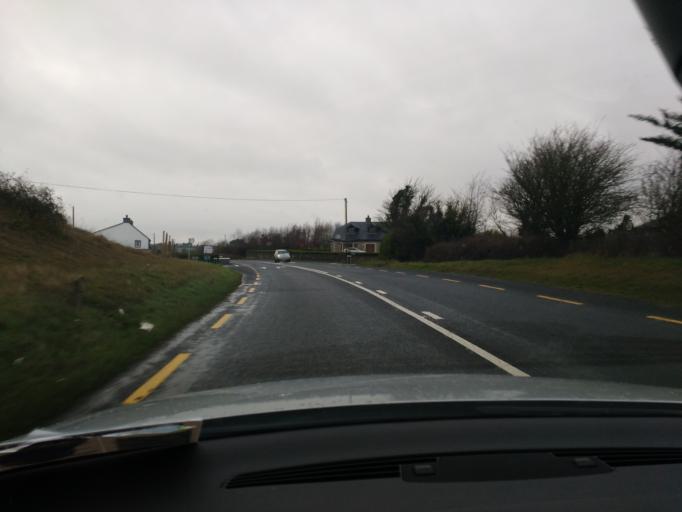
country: IE
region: Munster
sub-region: North Tipperary
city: Nenagh
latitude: 52.8349
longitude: -8.1263
